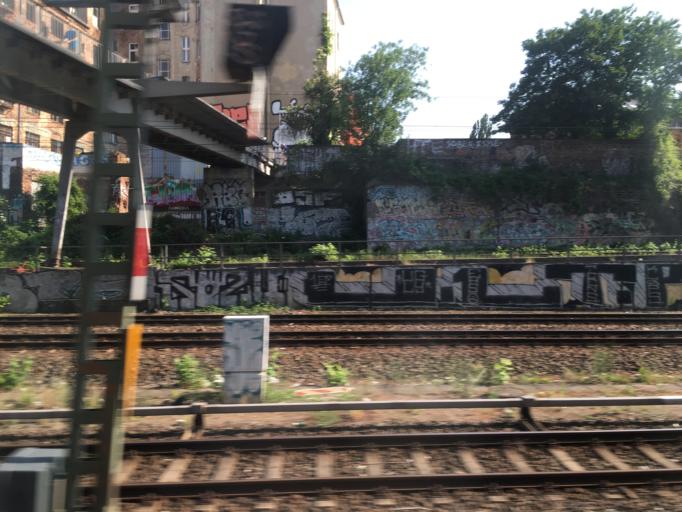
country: DE
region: Berlin
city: Gesundbrunnen
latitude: 52.5498
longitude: 13.4080
